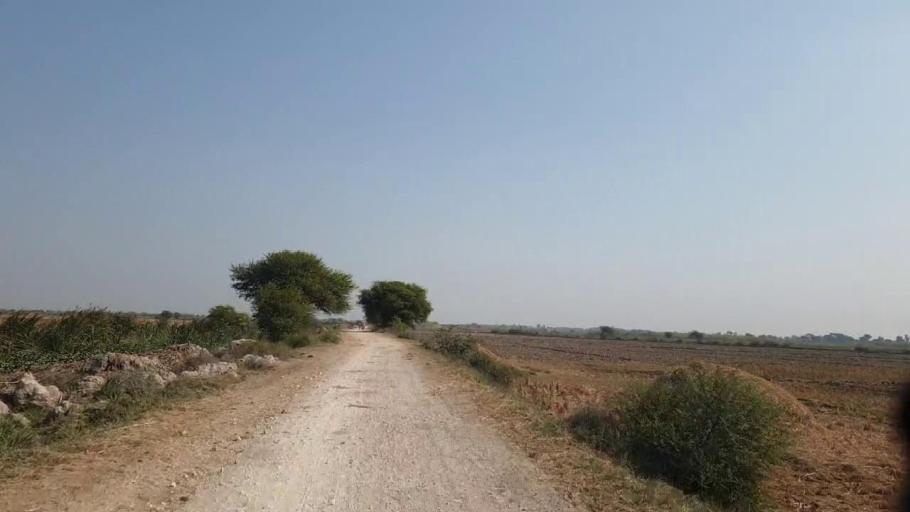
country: PK
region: Sindh
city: Tando Muhammad Khan
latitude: 25.0838
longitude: 68.4289
